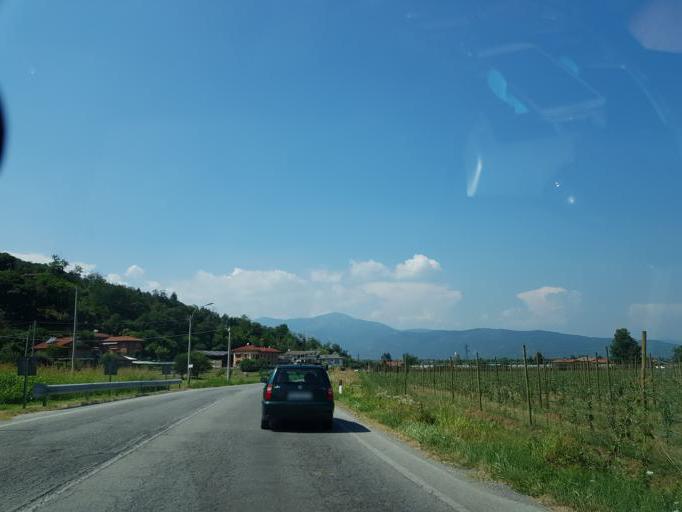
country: IT
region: Piedmont
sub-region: Provincia di Cuneo
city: Caraglio
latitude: 44.4261
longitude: 7.4274
